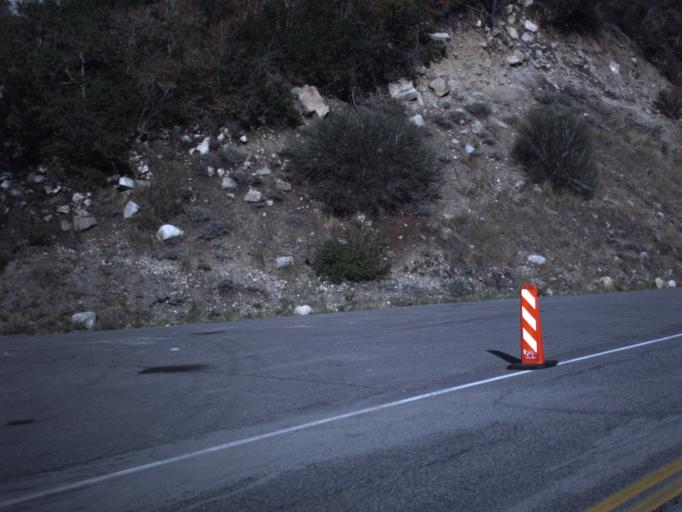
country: US
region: Utah
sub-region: Salt Lake County
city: Granite
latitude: 40.5714
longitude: -111.7170
